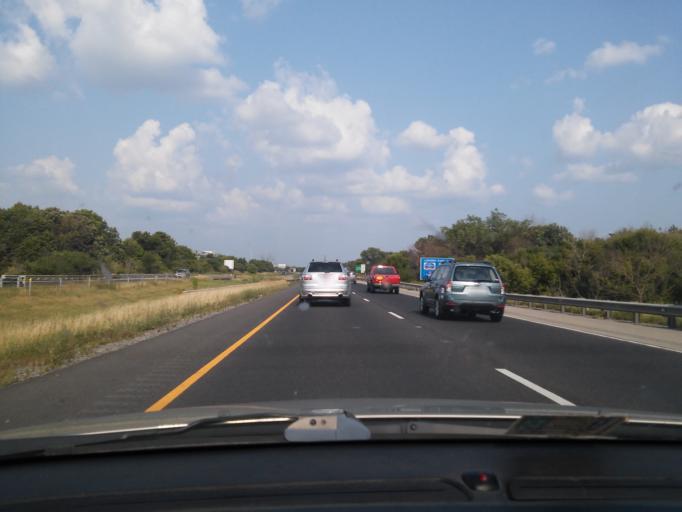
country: US
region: Illinois
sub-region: Will County
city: Shorewood
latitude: 41.4865
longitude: -88.1878
